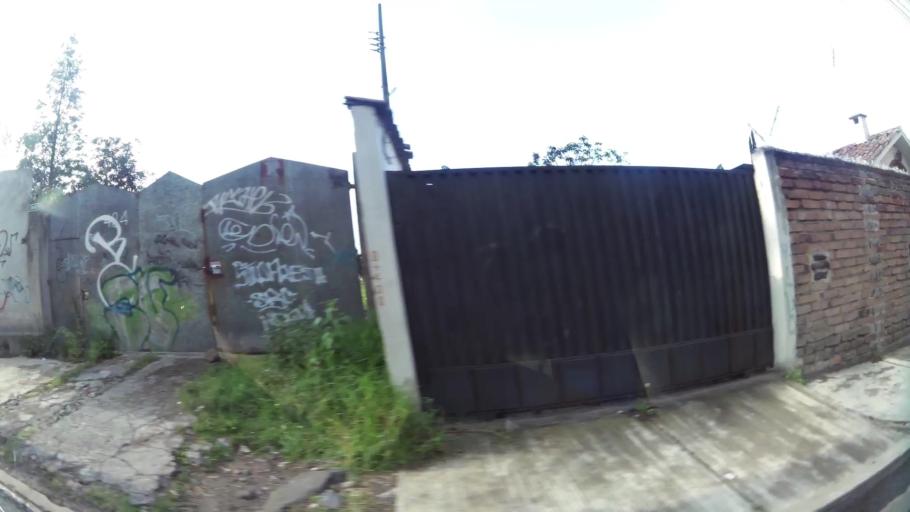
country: EC
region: Pichincha
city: Sangolqui
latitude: -0.2993
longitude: -78.4659
